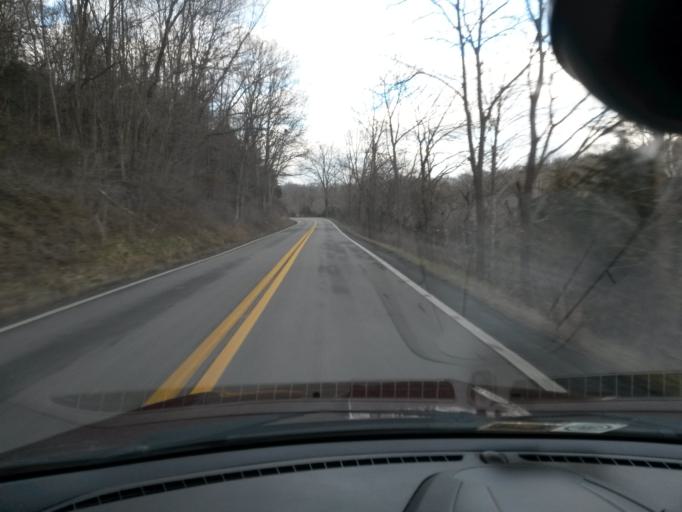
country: US
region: West Virginia
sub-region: Monroe County
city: Union
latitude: 37.5624
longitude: -80.5692
